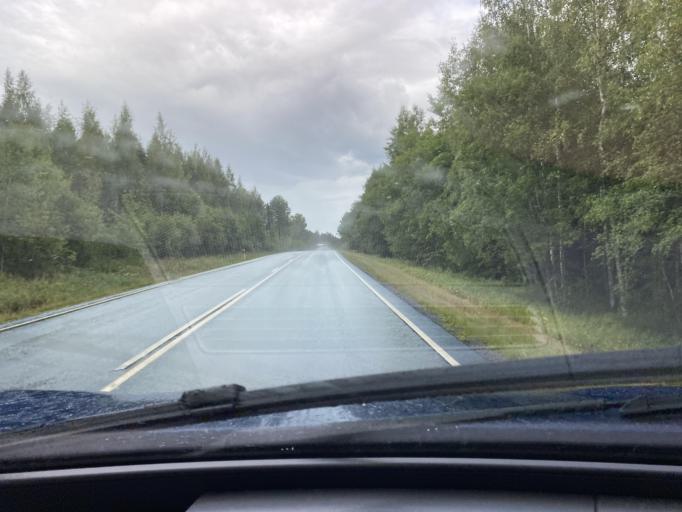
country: FI
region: Pirkanmaa
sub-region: Tampere
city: Haemeenkyroe
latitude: 61.6180
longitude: 23.1262
